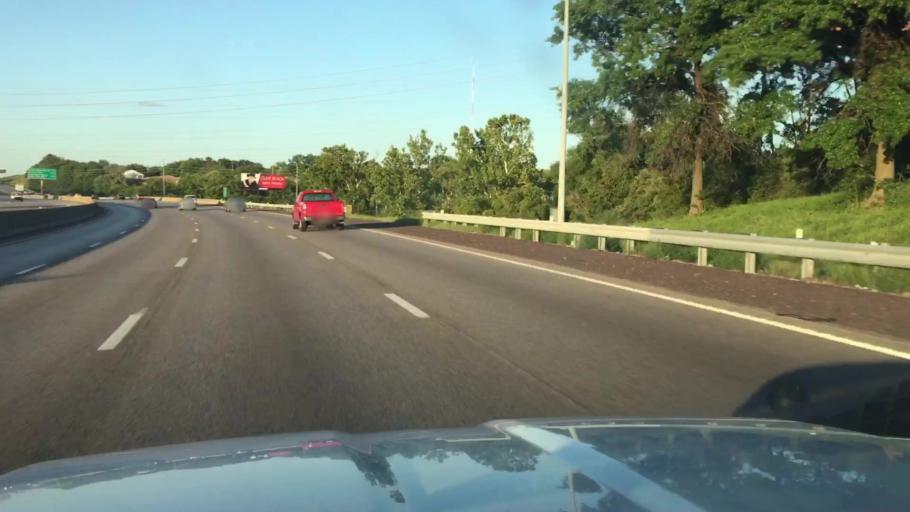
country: US
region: Missouri
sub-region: Saint Louis County
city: Mehlville
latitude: 38.5223
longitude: -90.3224
